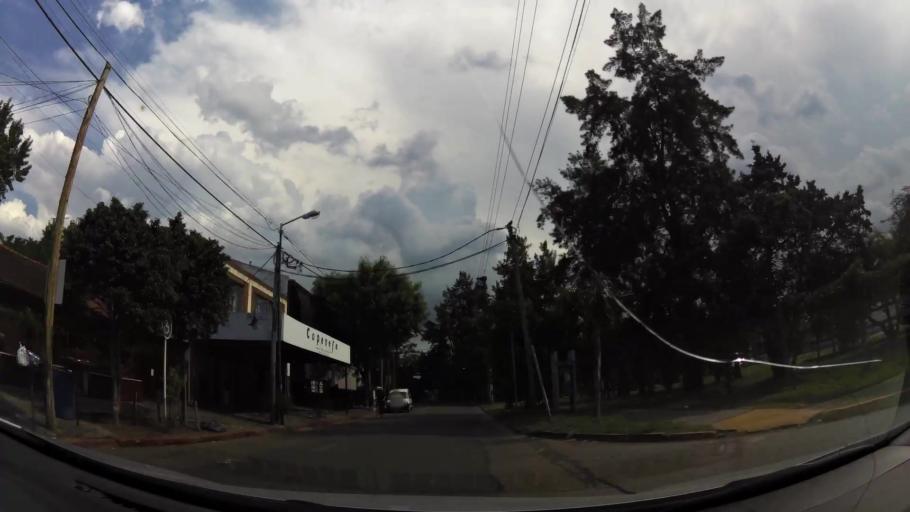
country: AR
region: Buenos Aires
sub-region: Partido de Tigre
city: Tigre
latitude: -34.4717
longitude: -58.5773
